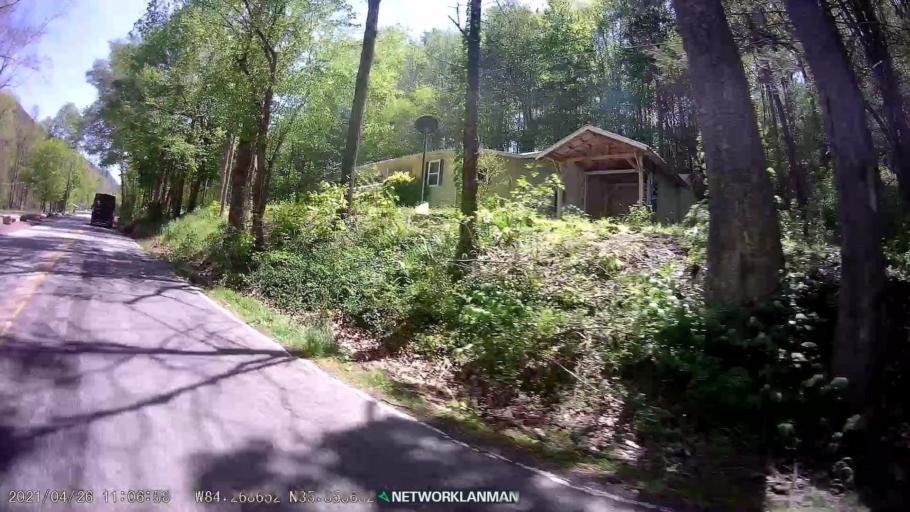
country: US
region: Tennessee
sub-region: Monroe County
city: Madisonville
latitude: 35.3556
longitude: -84.2686
